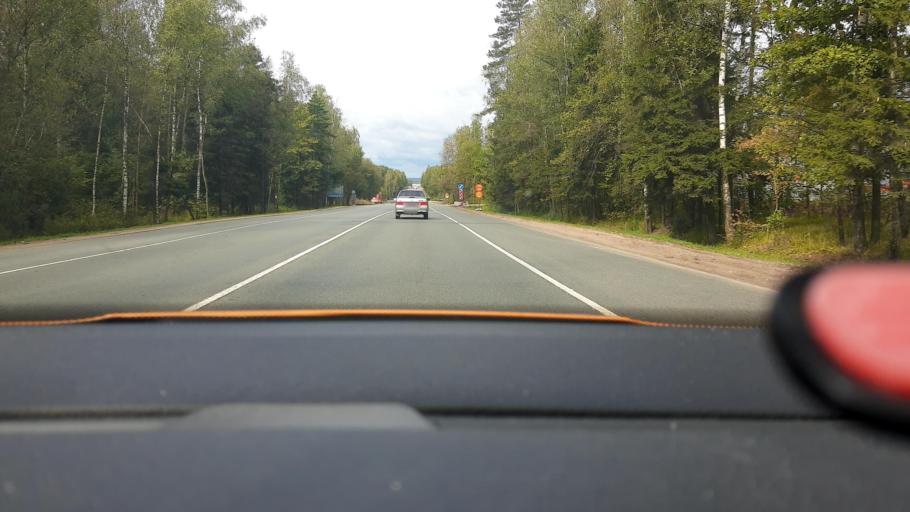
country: RU
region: Moskovskaya
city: Zelenogradskiy
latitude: 56.0961
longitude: 37.9788
